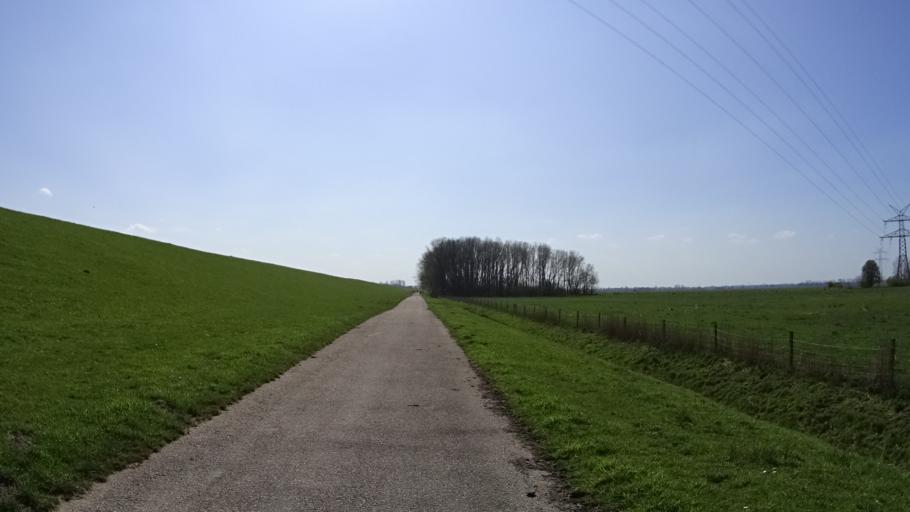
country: DE
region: Lower Saxony
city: Weener
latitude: 53.1477
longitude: 7.3703
